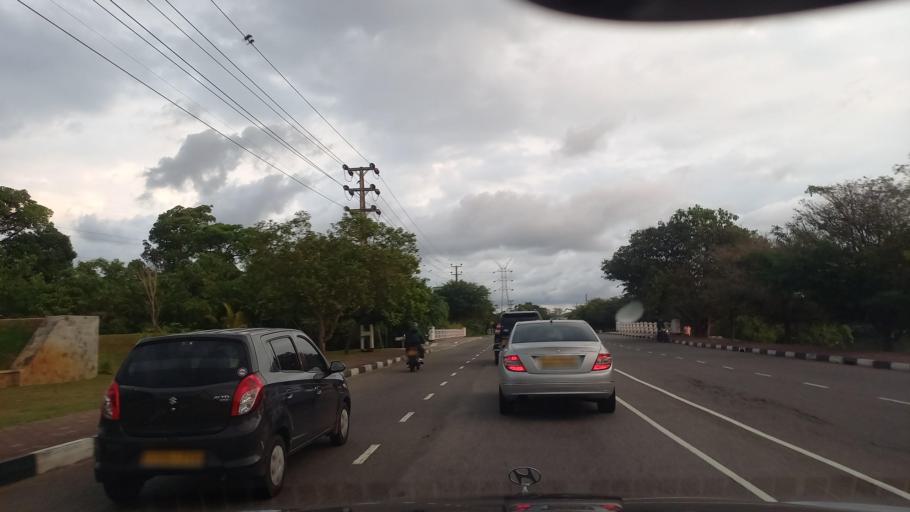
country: LK
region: Western
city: Battaramulla South
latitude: 6.8796
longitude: 79.9284
